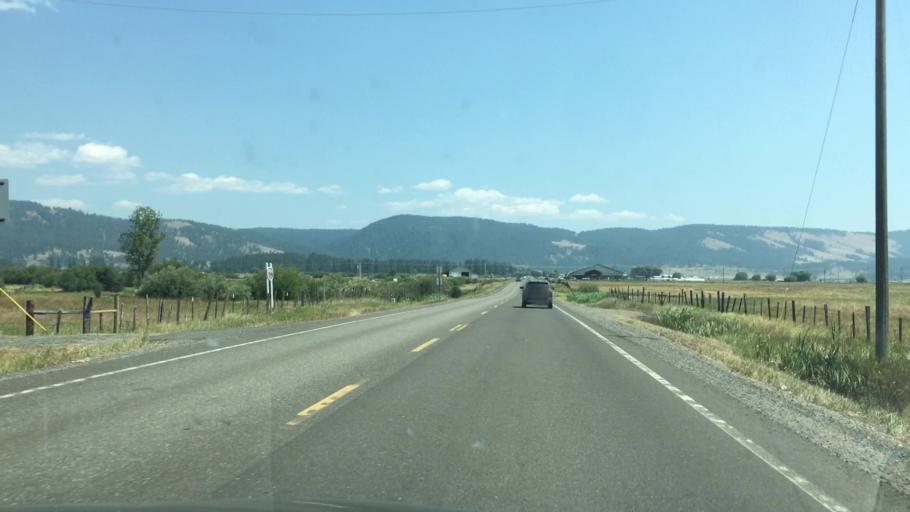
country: US
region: Idaho
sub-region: Valley County
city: McCall
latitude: 44.9701
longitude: -116.2768
